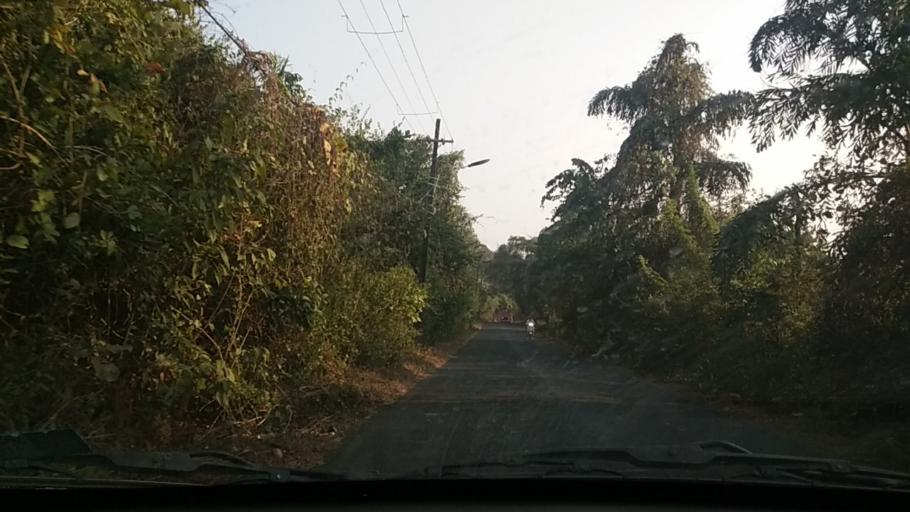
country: IN
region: Goa
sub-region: North Goa
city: Bambolim
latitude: 15.4660
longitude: 73.8762
